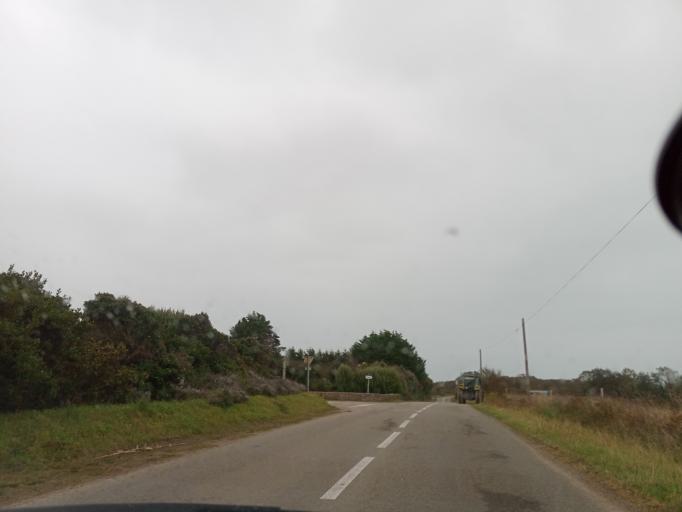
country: FR
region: Brittany
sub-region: Departement du Finistere
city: Esquibien
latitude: 48.0185
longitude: -4.5581
